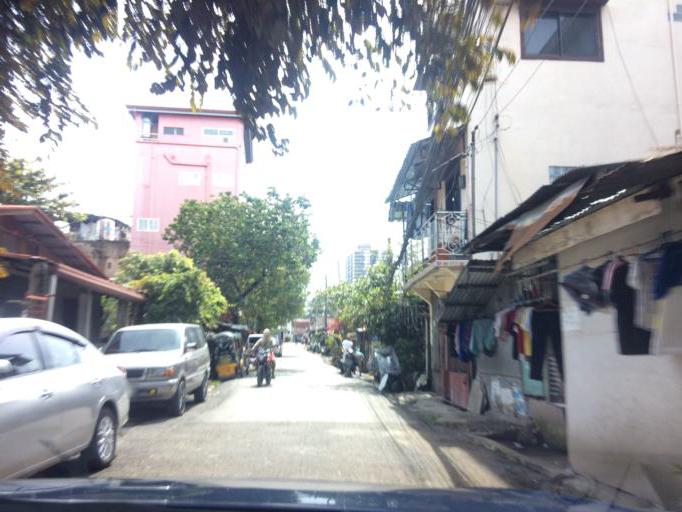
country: PH
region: Central Visayas
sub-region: Province of Cebu
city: Cebu City
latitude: 10.3212
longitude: 123.8946
